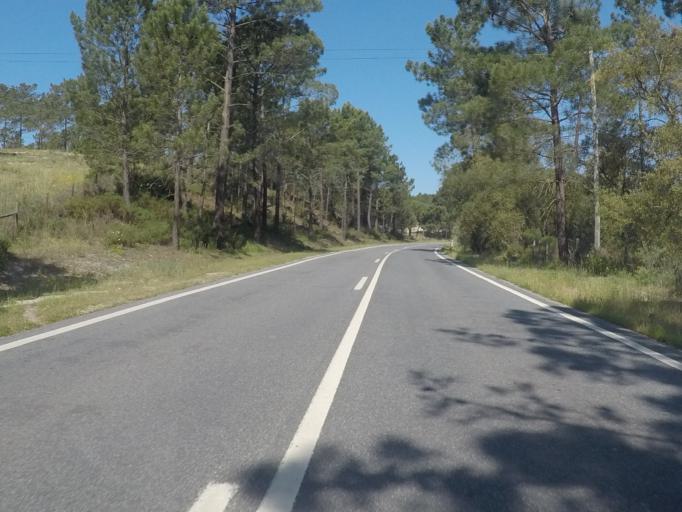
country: PT
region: Setubal
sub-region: Grandola
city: Grandola
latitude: 38.3011
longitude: -8.7323
